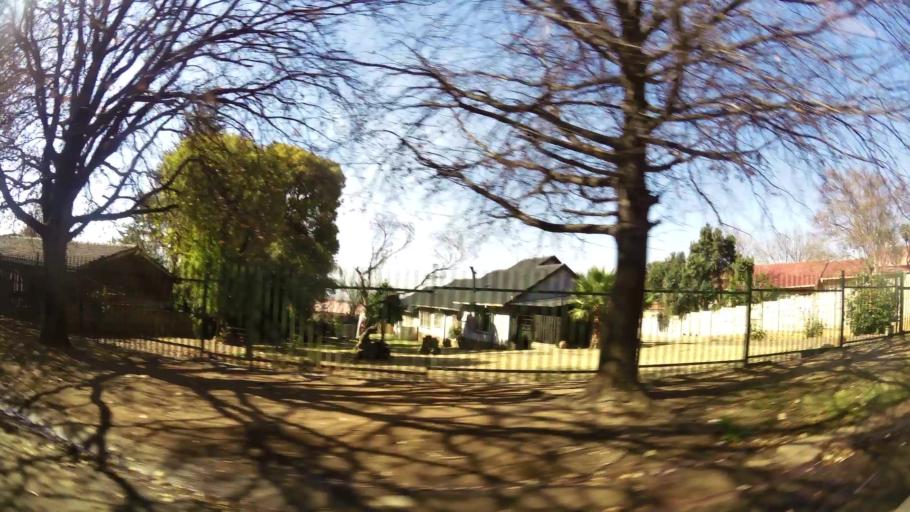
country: ZA
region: Mpumalanga
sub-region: Nkangala District Municipality
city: Witbank
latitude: -25.8317
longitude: 29.2463
